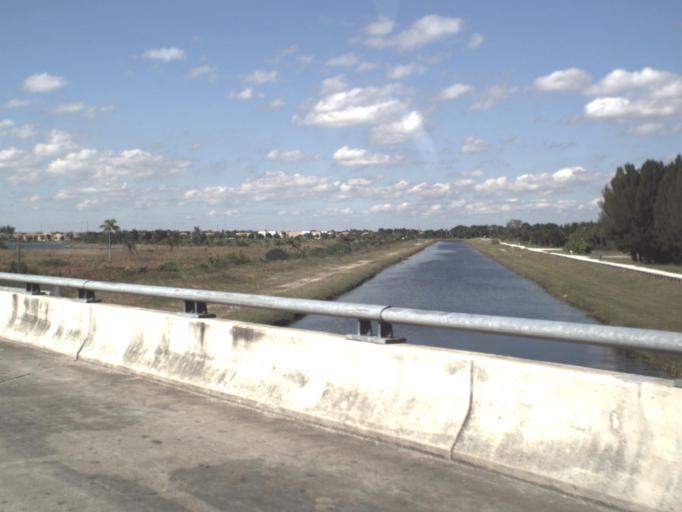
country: US
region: Florida
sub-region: Miami-Dade County
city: Country Club
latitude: 25.9642
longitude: -80.3328
